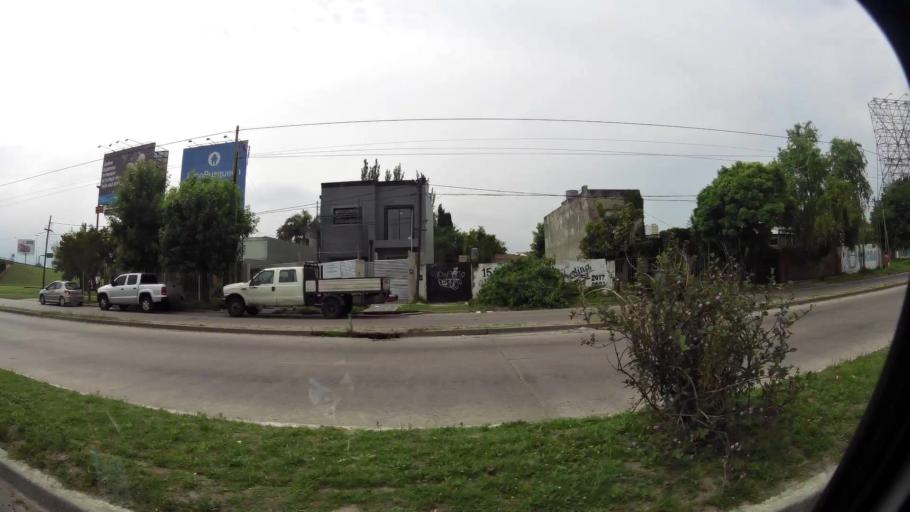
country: AR
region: Buenos Aires
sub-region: Partido de La Plata
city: La Plata
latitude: -34.8975
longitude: -57.9906
